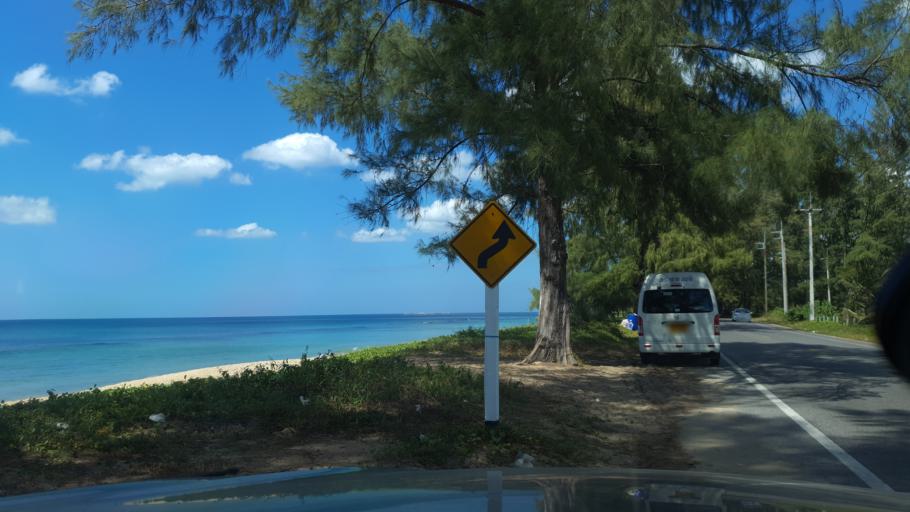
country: TH
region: Phangnga
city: Thai Mueang
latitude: 8.2962
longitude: 98.2718
